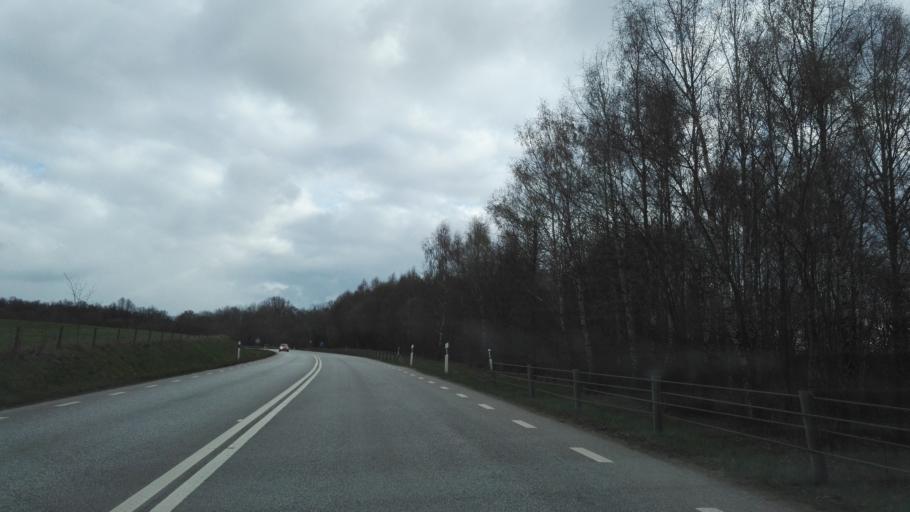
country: SE
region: Skane
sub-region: Horby Kommun
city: Hoerby
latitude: 55.8761
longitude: 13.6319
